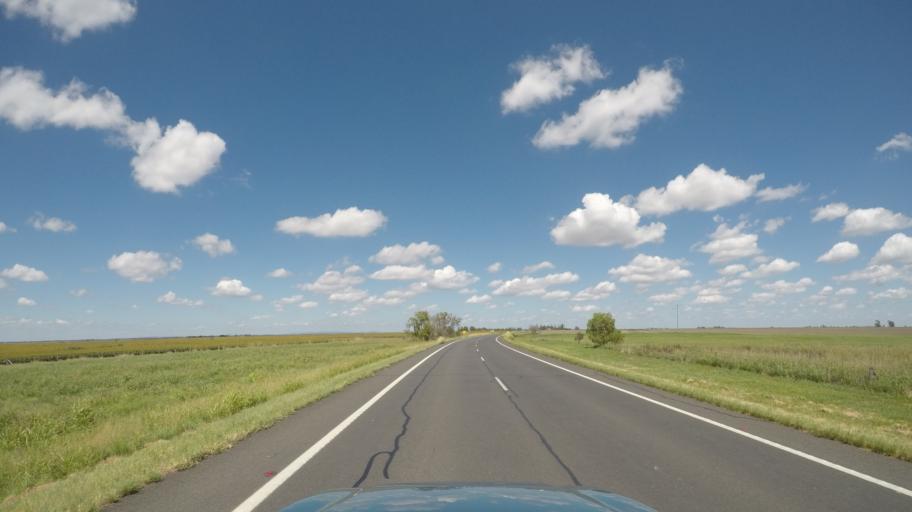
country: AU
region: Queensland
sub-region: Toowoomba
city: Westbrook
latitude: -27.7563
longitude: 151.5069
